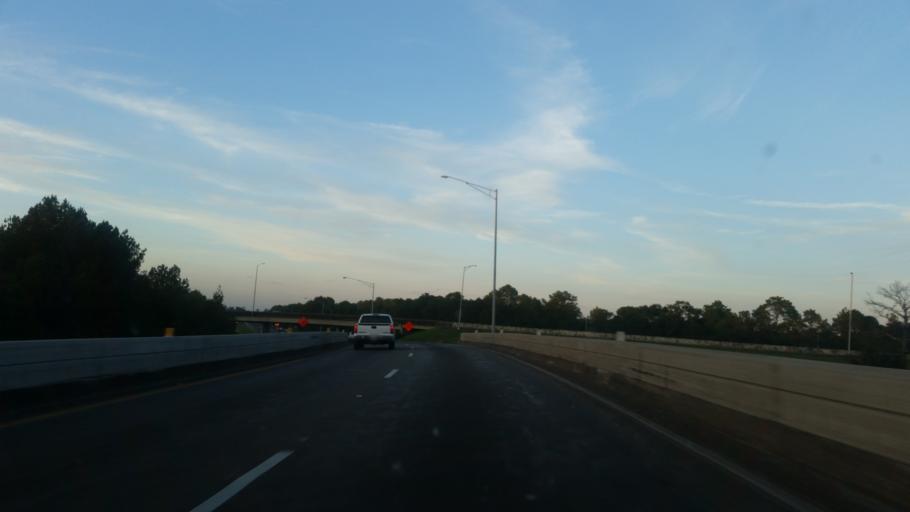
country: US
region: Alabama
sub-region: Mobile County
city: Tillmans Corner
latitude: 30.6283
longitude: -88.1179
